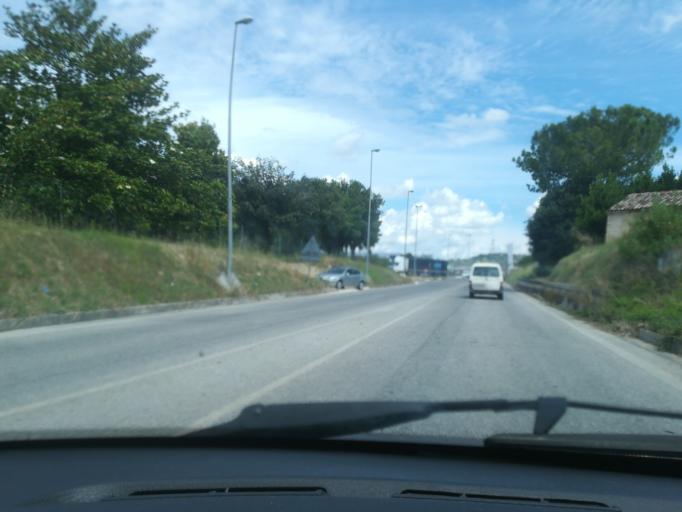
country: IT
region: The Marches
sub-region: Provincia di Macerata
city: Santa Maria Apparente
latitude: 43.2802
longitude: 13.6853
